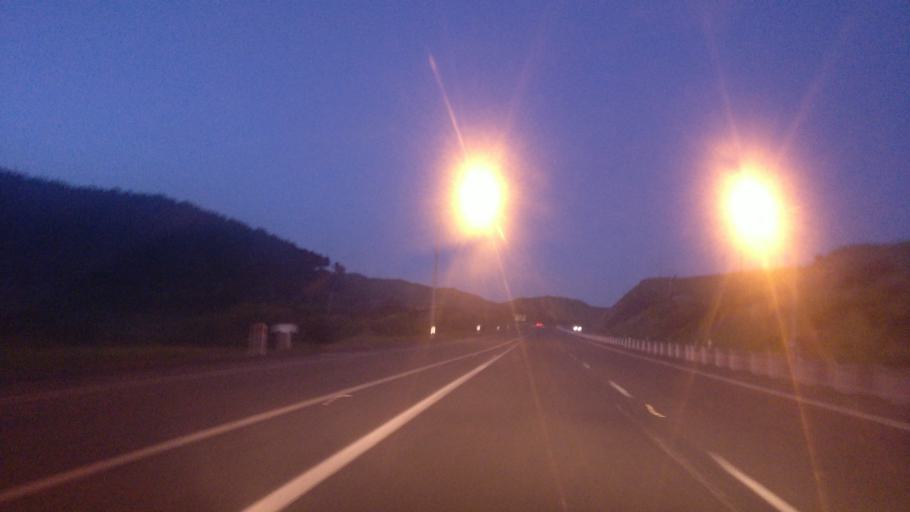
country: NZ
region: Wellington
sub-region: Porirua City
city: Porirua
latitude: -41.0747
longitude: 174.8748
